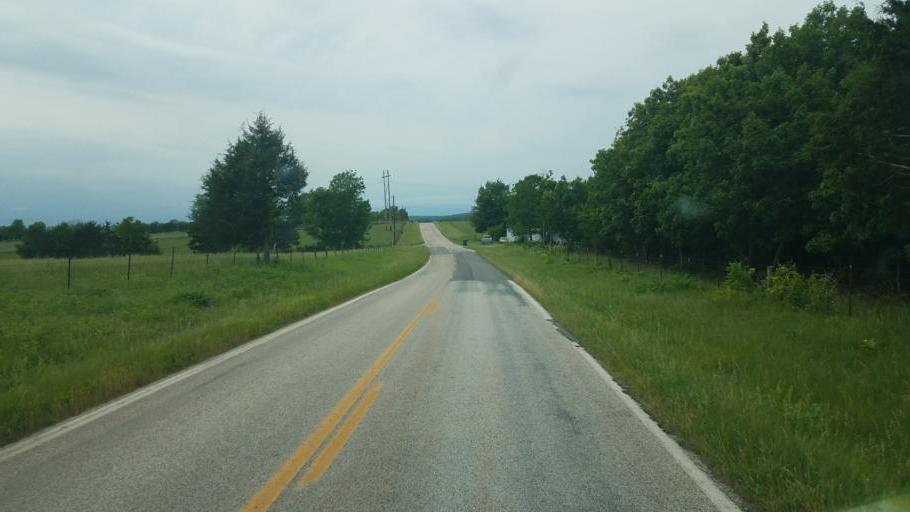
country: US
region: Missouri
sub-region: Moniteau County
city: California
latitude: 38.6838
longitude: -92.5966
